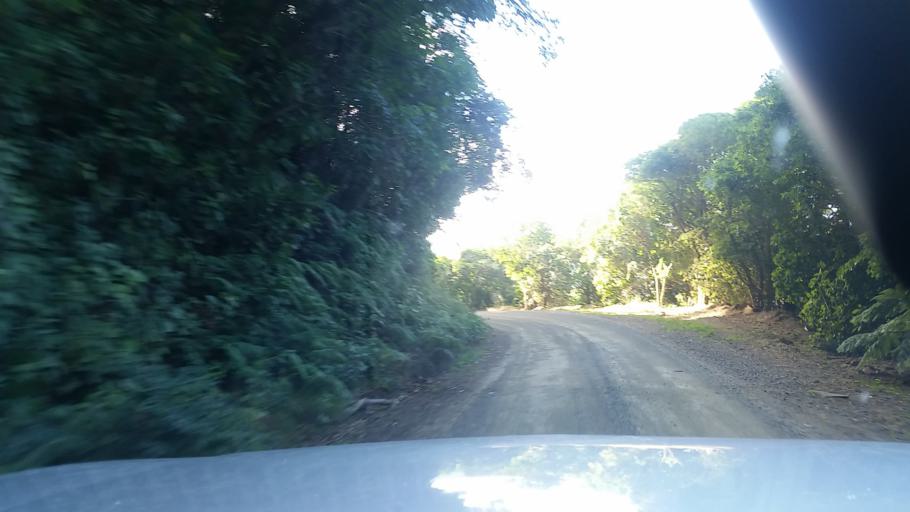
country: NZ
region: Marlborough
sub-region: Marlborough District
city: Picton
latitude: -41.2884
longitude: 174.1718
